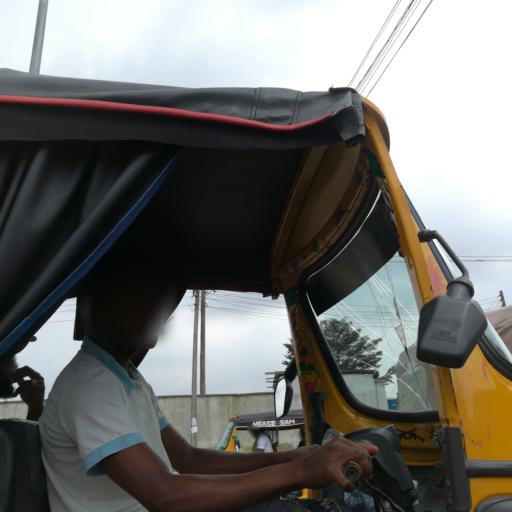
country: NG
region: Rivers
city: Port Harcourt
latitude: 4.8302
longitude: 7.0710
